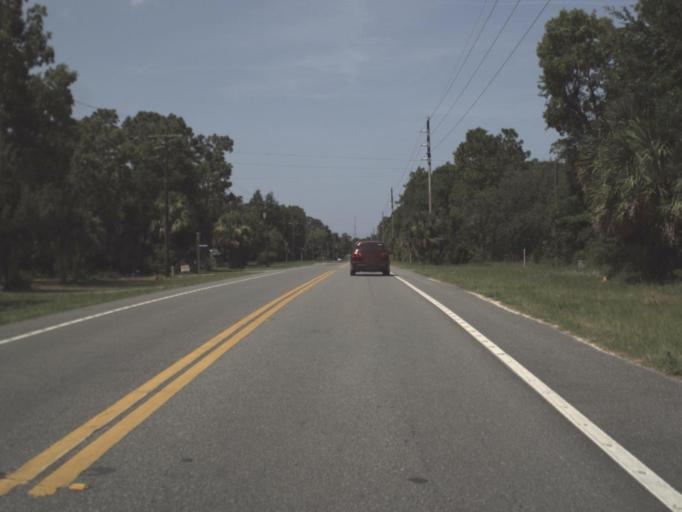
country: US
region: Florida
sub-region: Taylor County
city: Steinhatchee
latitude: 29.6817
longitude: -83.3638
